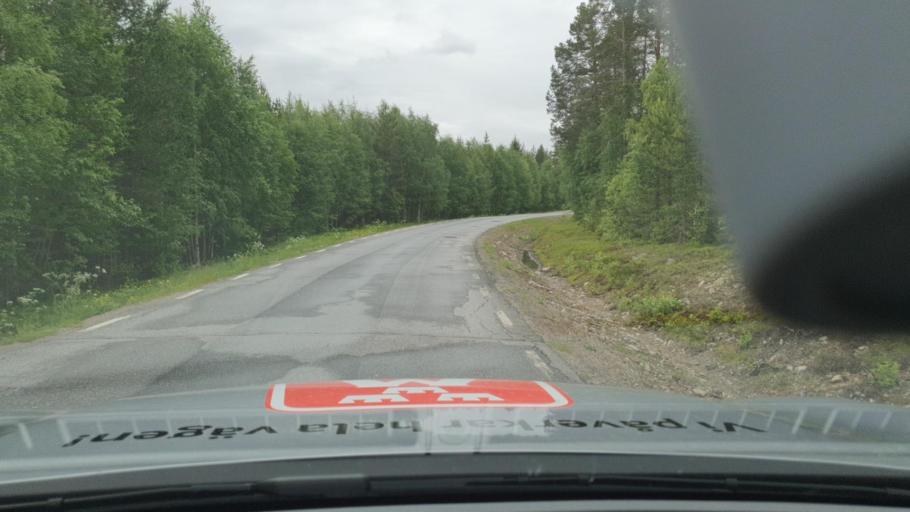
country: SE
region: Norrbotten
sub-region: Lulea Kommun
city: Ranea
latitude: 65.7841
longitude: 22.2966
